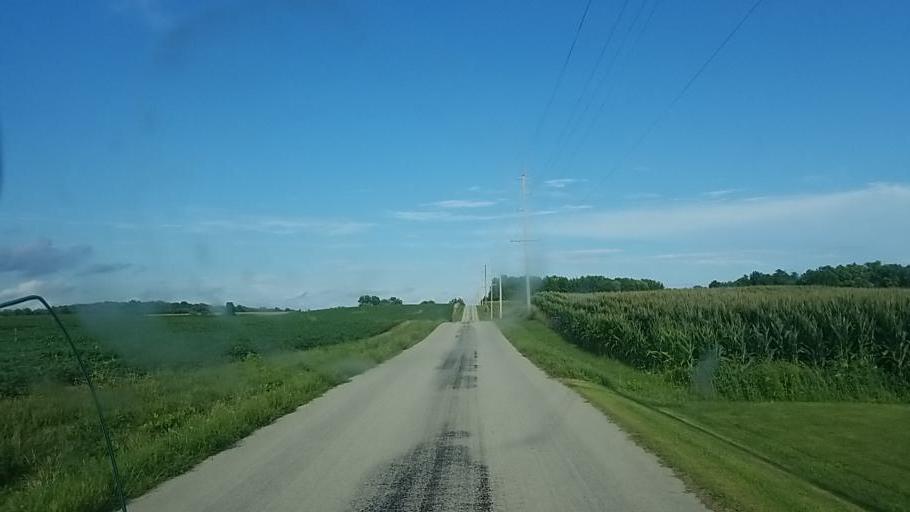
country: US
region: Ohio
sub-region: Wyandot County
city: Upper Sandusky
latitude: 40.8147
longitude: -83.1868
